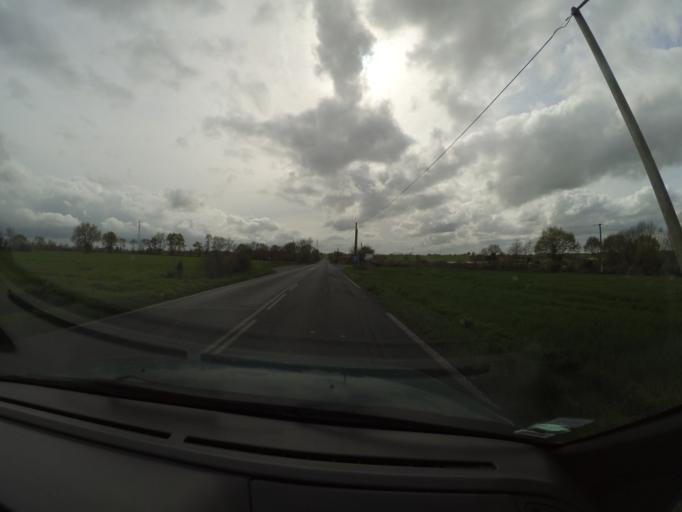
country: FR
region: Pays de la Loire
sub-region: Departement de Maine-et-Loire
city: Saint-Laurent-des-Autels
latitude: 47.2951
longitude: -1.1736
